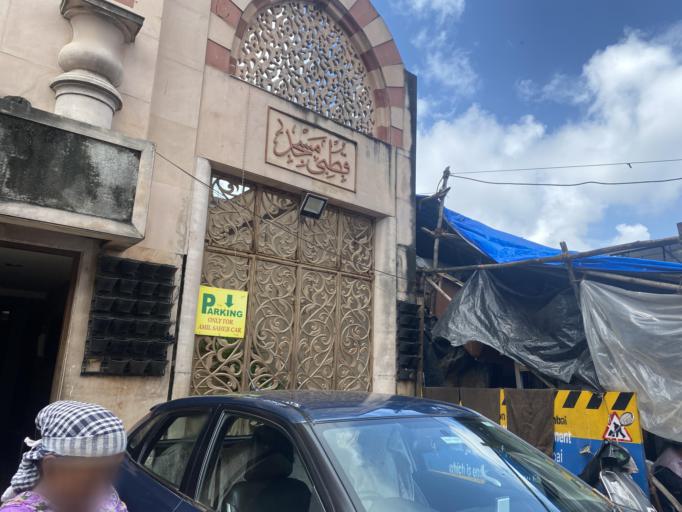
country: IN
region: Maharashtra
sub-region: Mumbai Suburban
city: Mumbai
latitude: 18.9598
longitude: 72.8302
